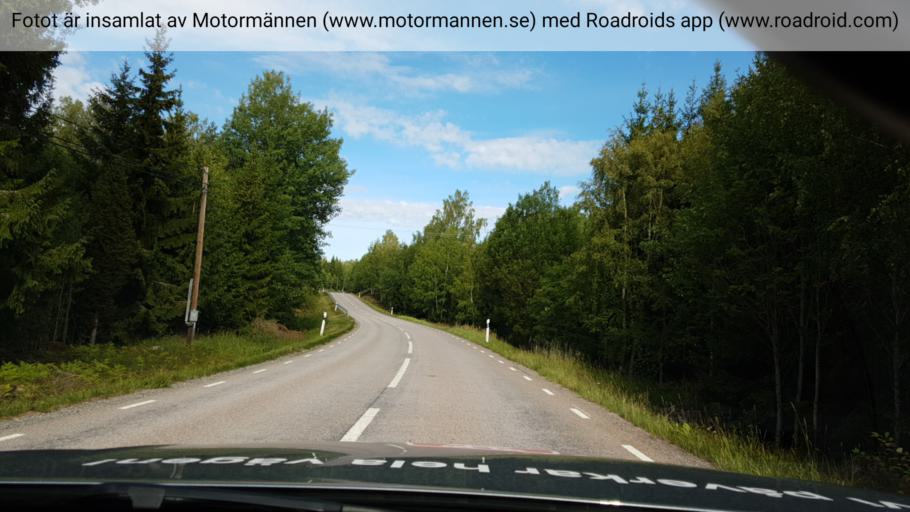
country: SE
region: Uppsala
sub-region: Heby Kommun
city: OEstervala
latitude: 60.0160
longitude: 17.2873
